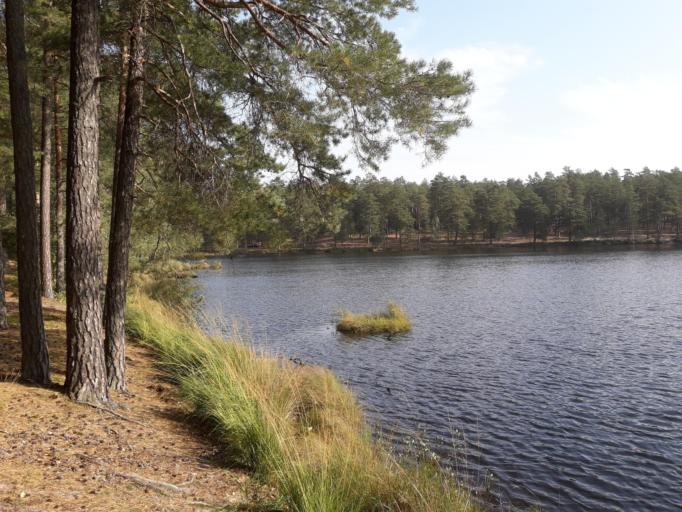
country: LT
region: Alytaus apskritis
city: Druskininkai
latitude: 54.0089
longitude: 24.0917
